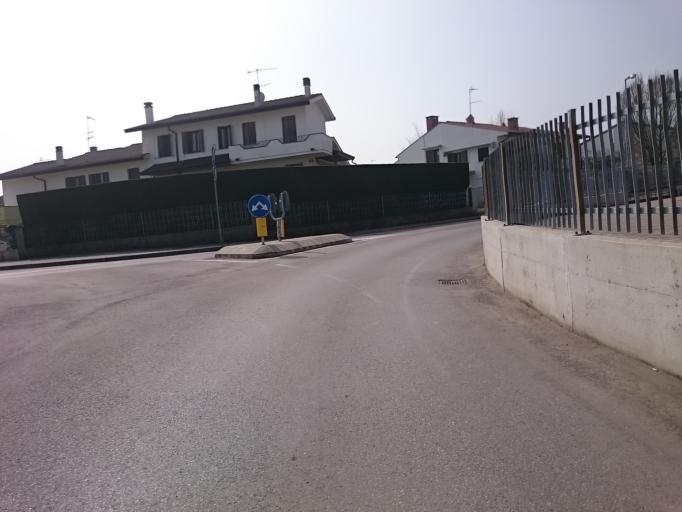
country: IT
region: Veneto
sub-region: Provincia di Padova
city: Monselice
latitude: 45.2405
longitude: 11.7690
